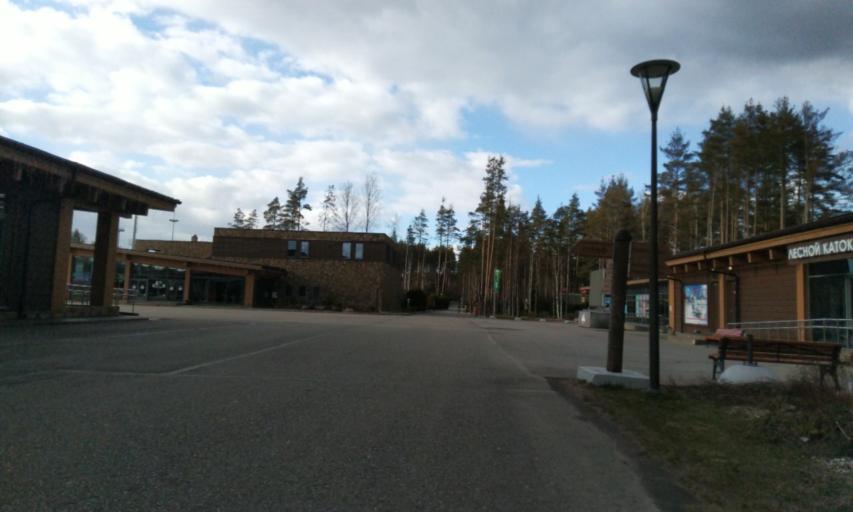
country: RU
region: Leningrad
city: Novoye Devyatkino
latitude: 60.1274
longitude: 30.4461
